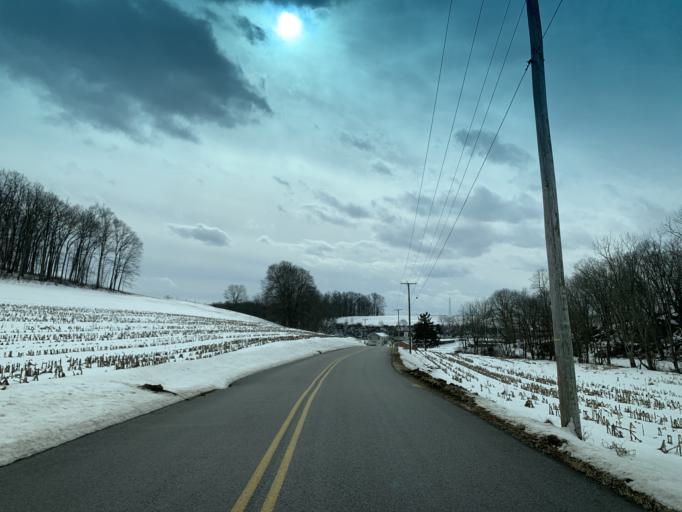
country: US
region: Pennsylvania
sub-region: York County
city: Shrewsbury
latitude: 39.7678
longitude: -76.6499
